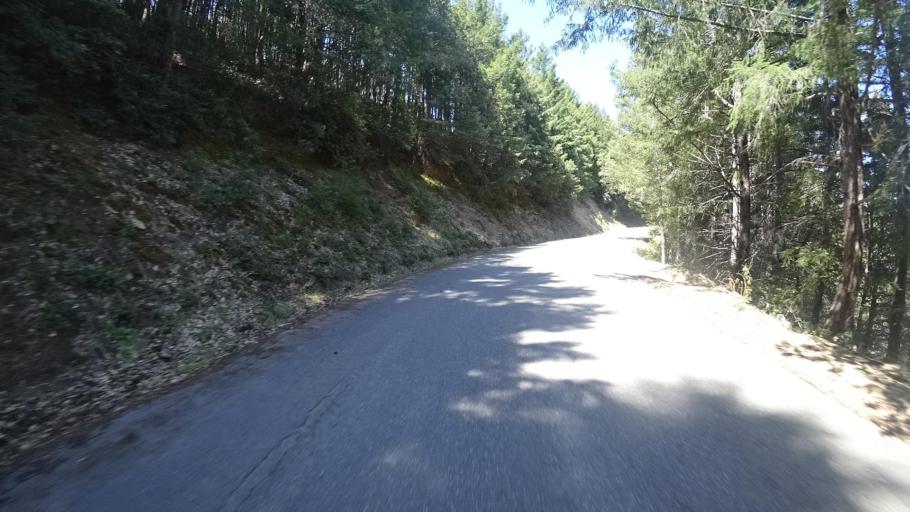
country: US
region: California
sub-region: Humboldt County
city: Redway
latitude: 40.1578
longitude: -124.0759
